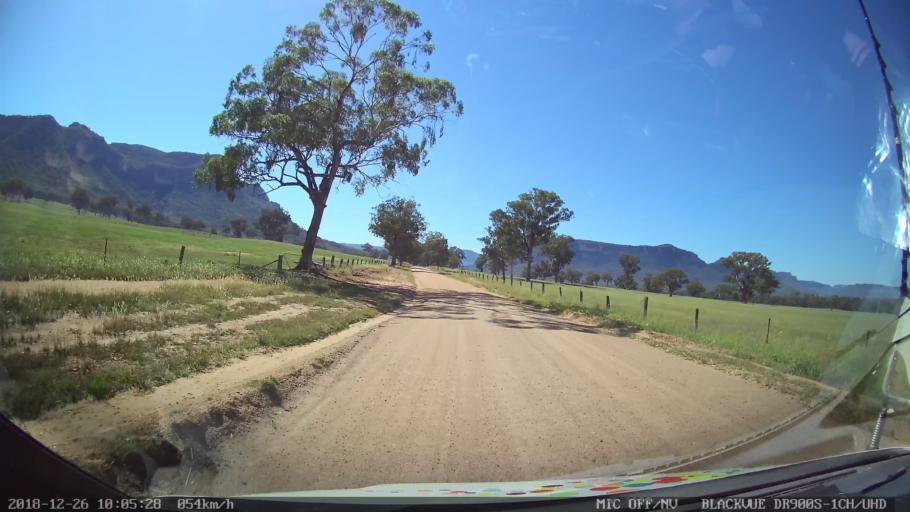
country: AU
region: New South Wales
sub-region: Mid-Western Regional
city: Kandos
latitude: -33.0780
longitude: 150.2119
